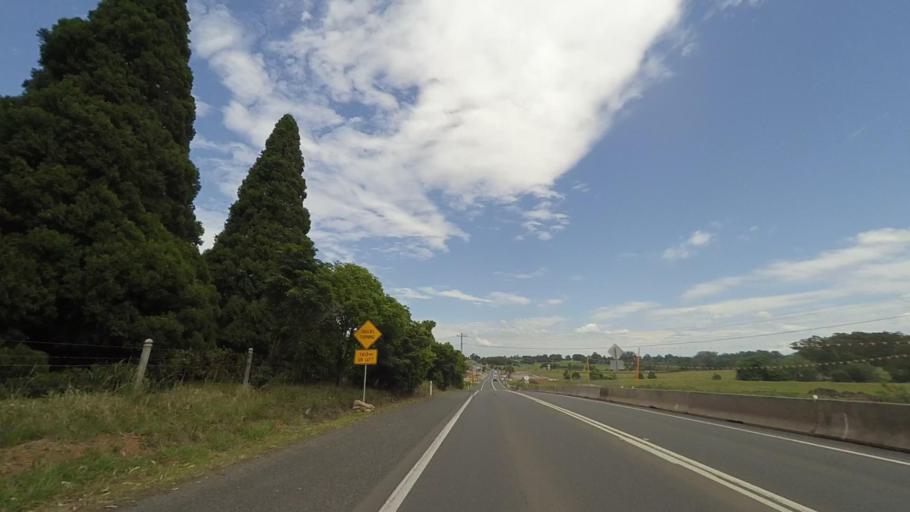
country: AU
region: New South Wales
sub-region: Shoalhaven Shire
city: Berry
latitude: -34.7835
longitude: 150.6779
